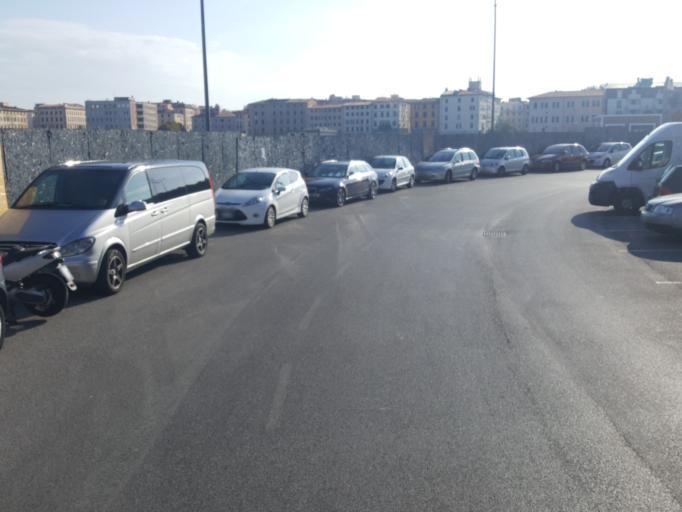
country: IT
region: Tuscany
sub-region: Provincia di Livorno
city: Livorno
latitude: 43.5453
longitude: 10.3004
